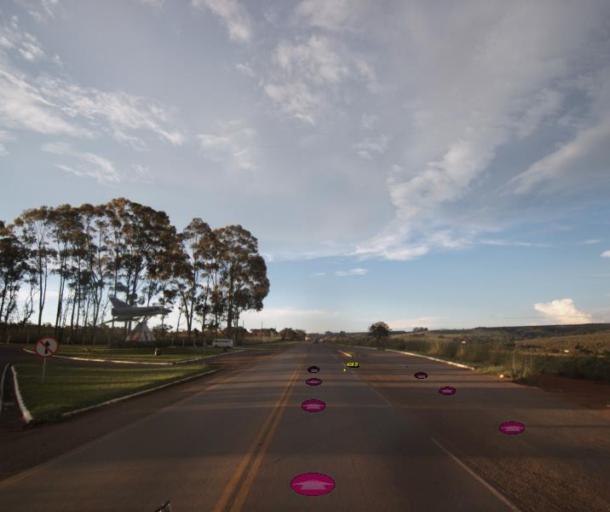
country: BR
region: Goias
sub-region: Anapolis
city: Anapolis
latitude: -16.2595
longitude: -48.9372
